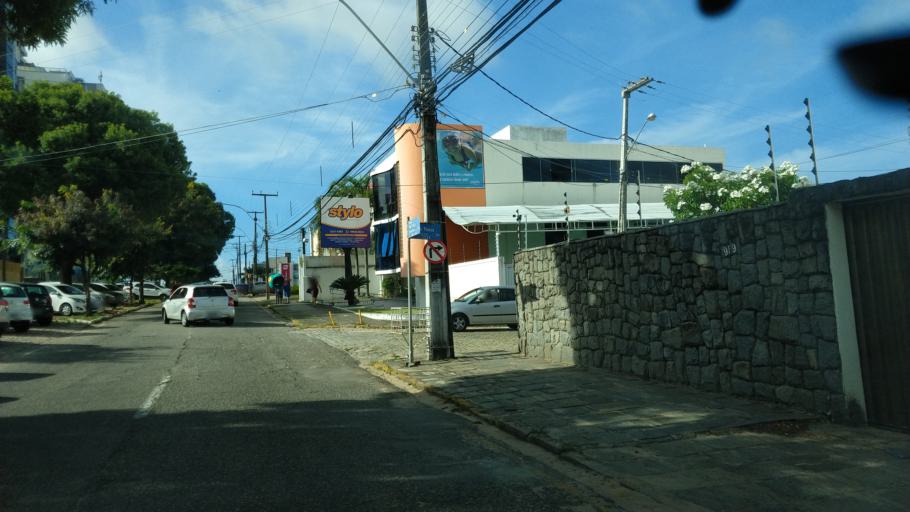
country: BR
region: Rio Grande do Norte
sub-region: Natal
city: Natal
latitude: -5.8120
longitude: -35.2016
